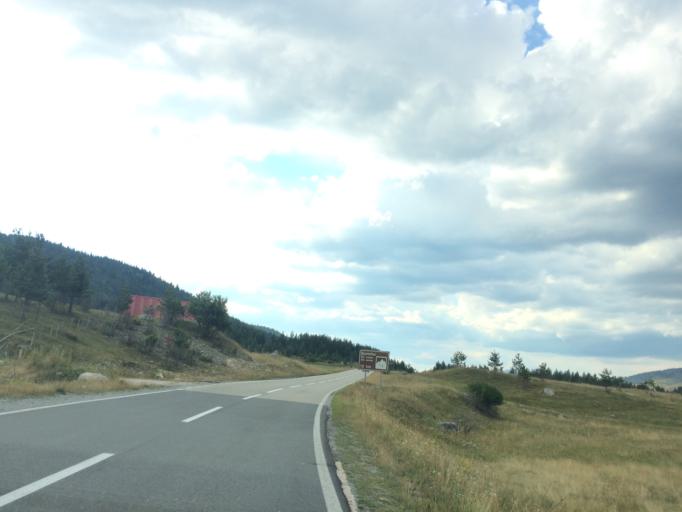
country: ME
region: Opstina Zabljak
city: Zabljak
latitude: 43.1436
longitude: 19.2259
